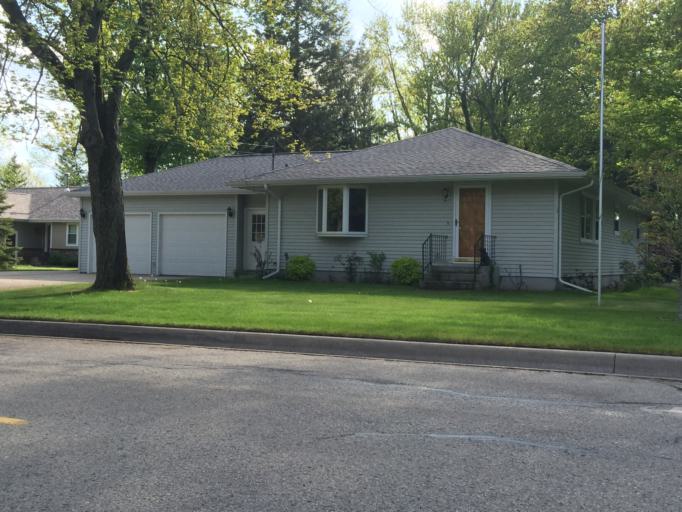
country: US
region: Michigan
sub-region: Menominee County
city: Menominee
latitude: 45.1397
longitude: -87.6175
